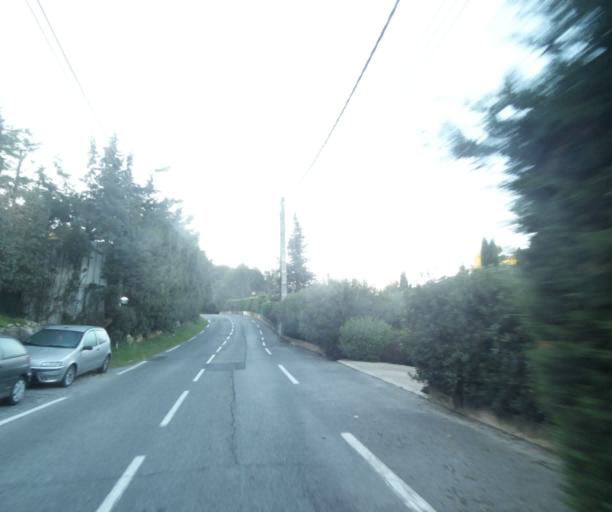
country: FR
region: Provence-Alpes-Cote d'Azur
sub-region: Departement des Alpes-Maritimes
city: Vallauris
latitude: 43.5851
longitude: 7.0814
